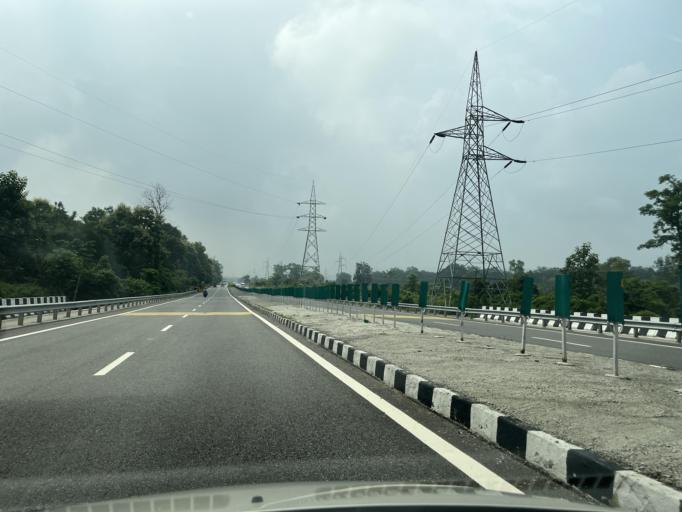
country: IN
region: Uttarakhand
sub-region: Dehradun
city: Raiwala
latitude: 30.0948
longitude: 78.1819
